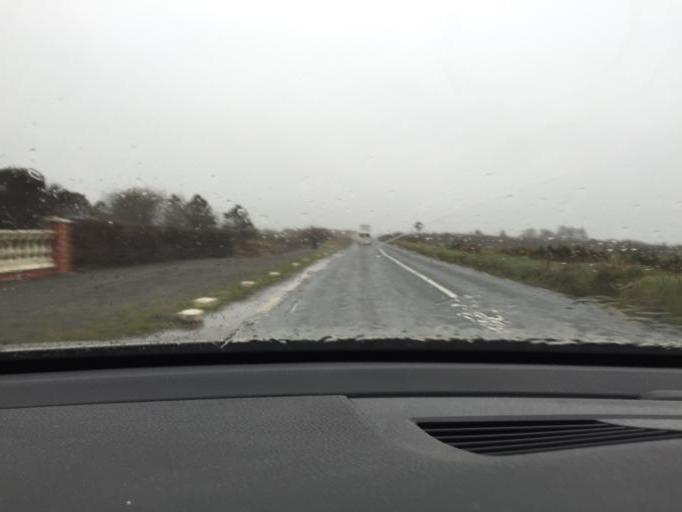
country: IE
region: Munster
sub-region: Ciarrai
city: Dingle
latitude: 52.1402
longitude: -10.2292
